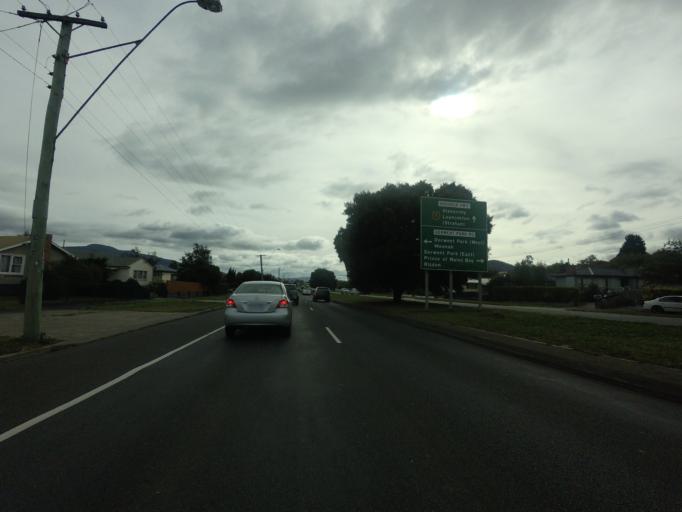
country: AU
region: Tasmania
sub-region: Glenorchy
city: Moonah
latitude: -42.8406
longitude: 147.3050
